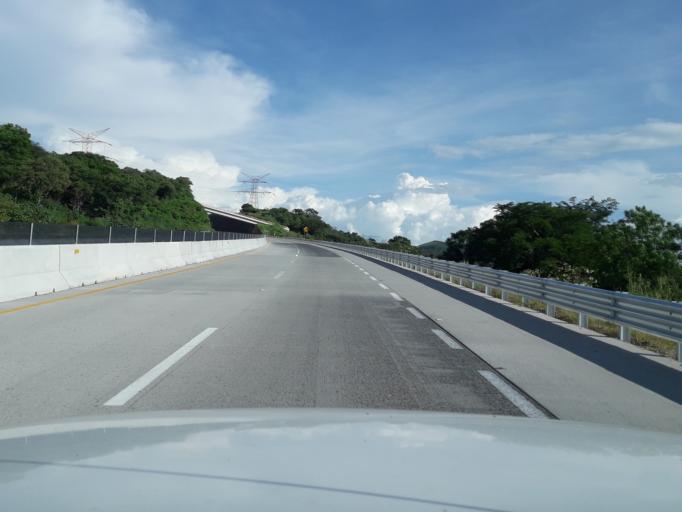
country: MX
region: Jalisco
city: Tala
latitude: 20.5865
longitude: -103.6694
